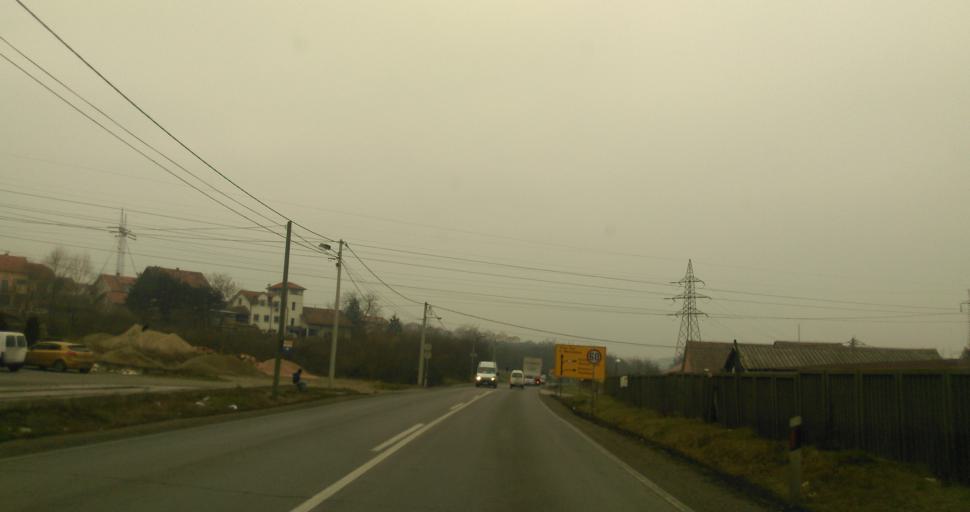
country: RS
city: Rusanj
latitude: 44.7165
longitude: 20.4685
